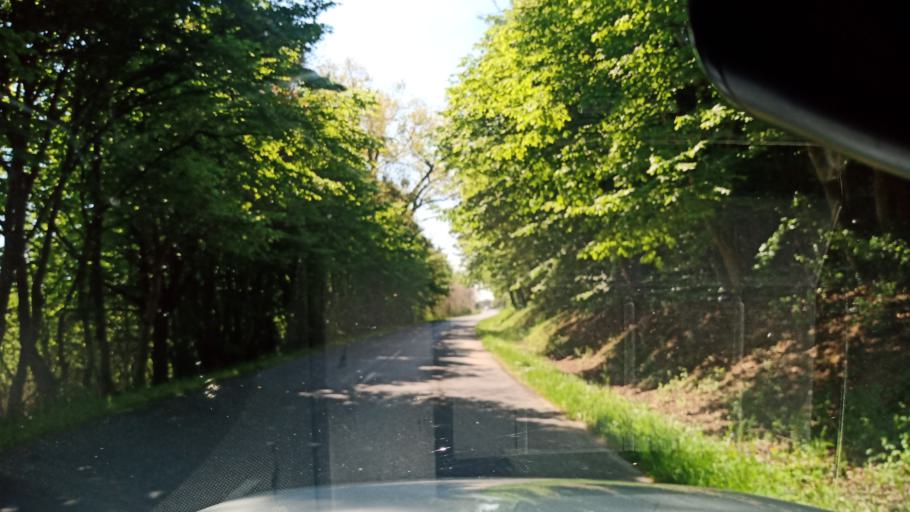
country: HU
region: Zala
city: Heviz
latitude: 46.7653
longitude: 17.1054
